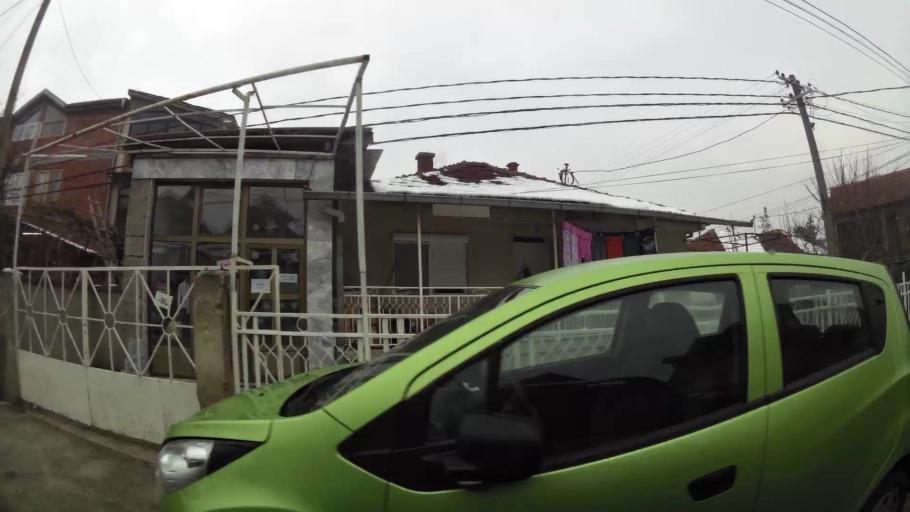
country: MK
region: Saraj
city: Saraj
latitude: 42.0371
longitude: 21.3488
